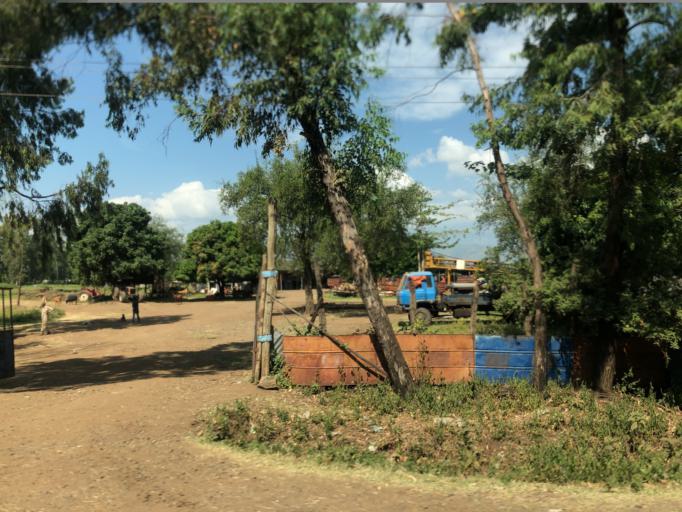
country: ET
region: Southern Nations, Nationalities, and People's Region
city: Arba Minch'
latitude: 5.8672
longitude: 37.4794
